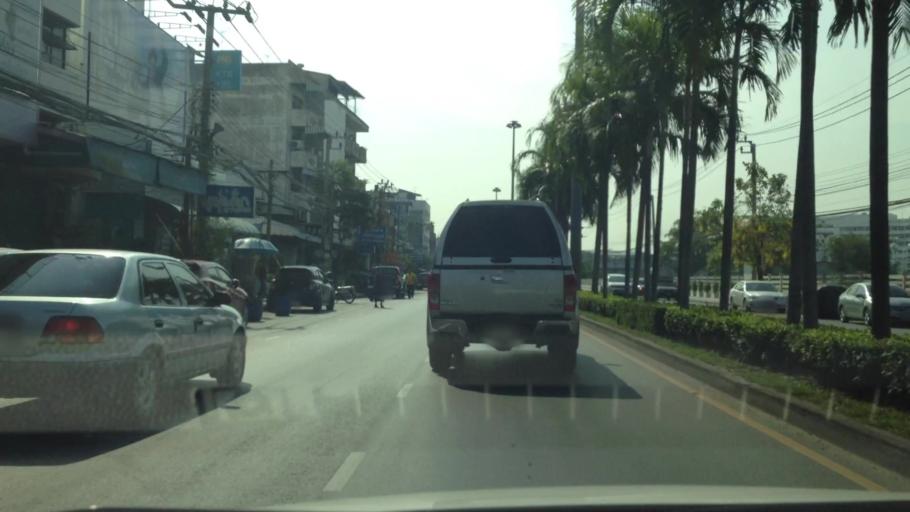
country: TH
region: Samut Prakan
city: Samut Prakan
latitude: 13.5893
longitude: 100.5977
